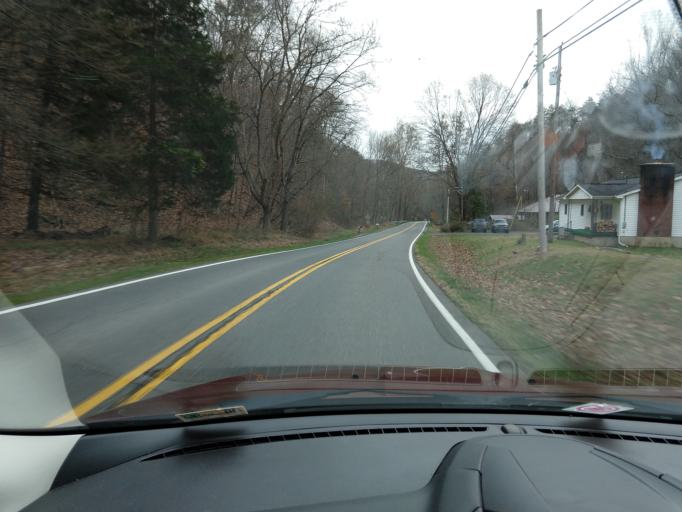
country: US
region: West Virginia
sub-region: Greenbrier County
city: White Sulphur Springs
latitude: 37.7389
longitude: -80.2241
